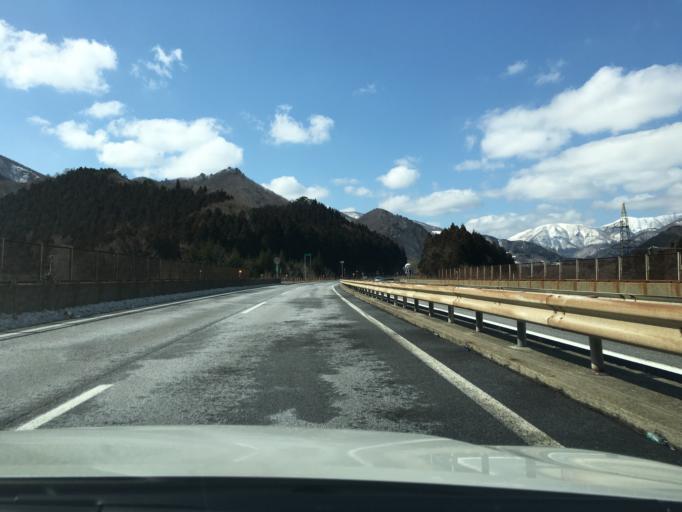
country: JP
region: Yamagata
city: Yamagata-shi
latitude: 38.2111
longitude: 140.5459
